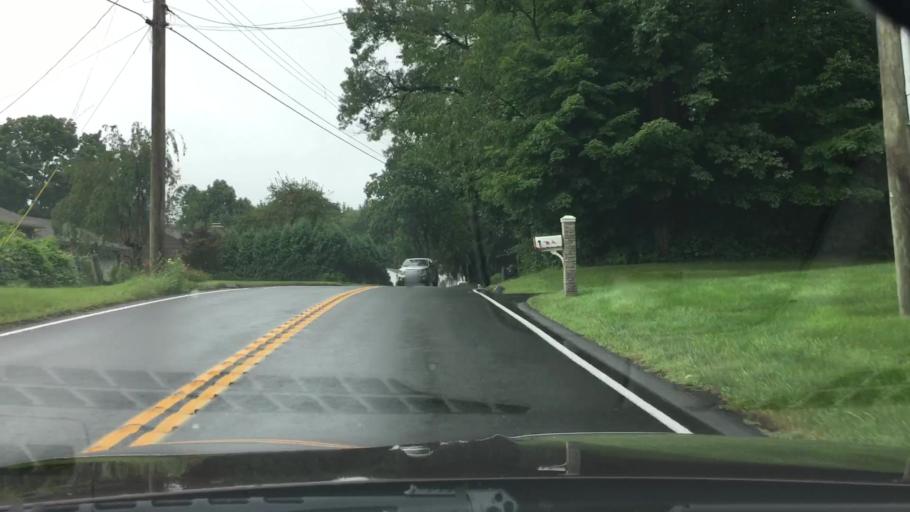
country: US
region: Connecticut
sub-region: Hartford County
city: Tariffville
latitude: 41.9361
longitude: -72.7505
